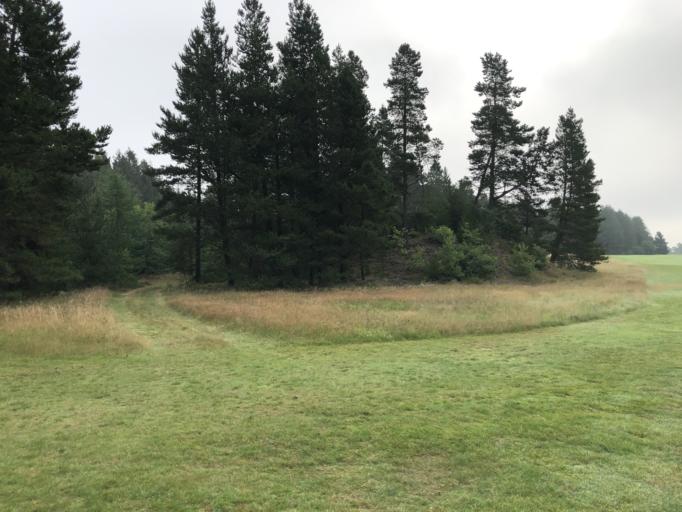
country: DK
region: Central Jutland
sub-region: Holstebro Kommune
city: Ulfborg
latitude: 56.3243
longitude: 8.4262
